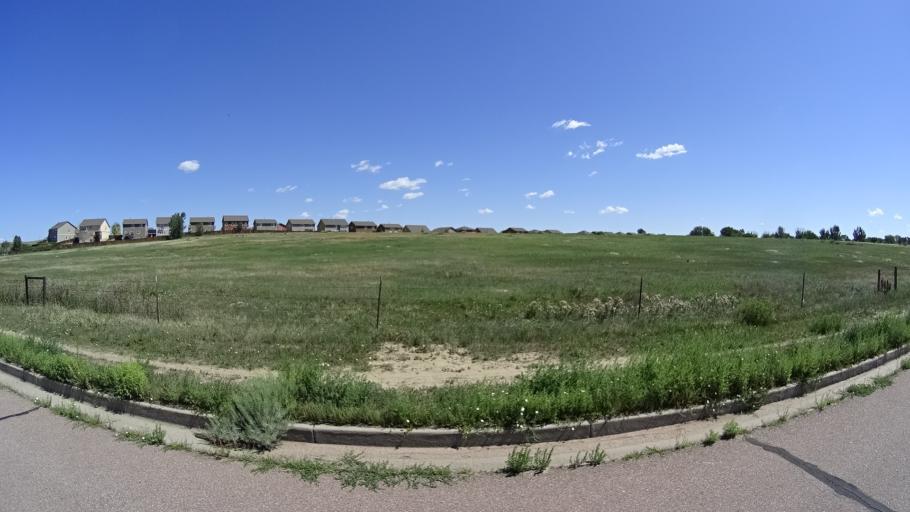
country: US
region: Colorado
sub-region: El Paso County
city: Security-Widefield
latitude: 38.7735
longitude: -104.6565
